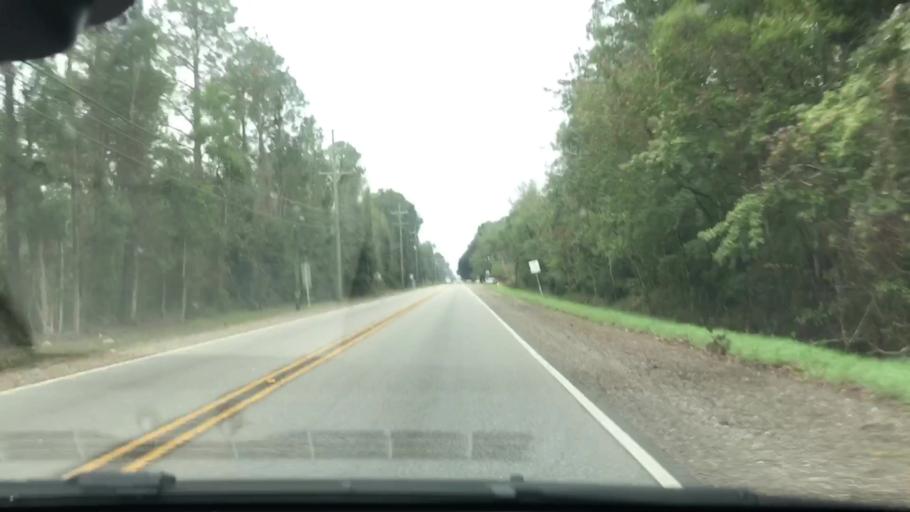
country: US
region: Louisiana
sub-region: Saint Tammany Parish
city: Pearl River
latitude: 30.3340
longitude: -89.7613
